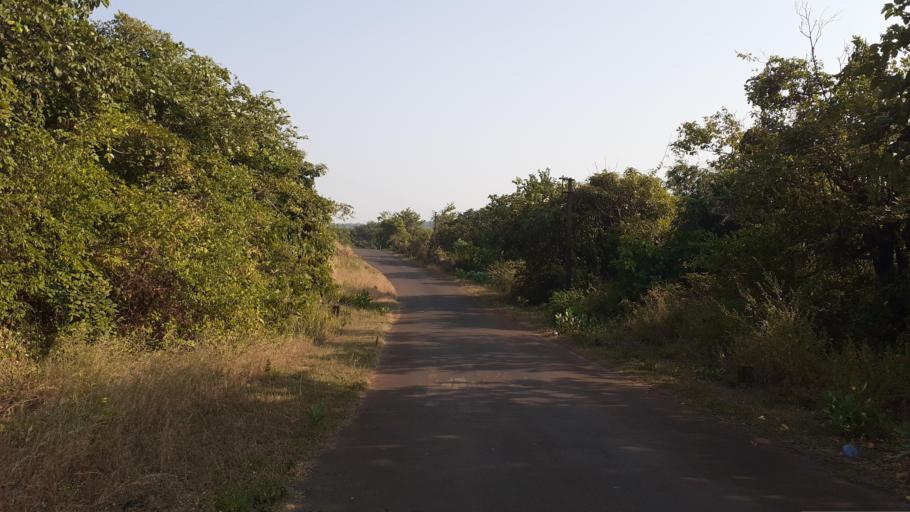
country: IN
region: Maharashtra
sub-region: Ratnagiri
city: Ratnagiri
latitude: 17.2197
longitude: 73.2463
